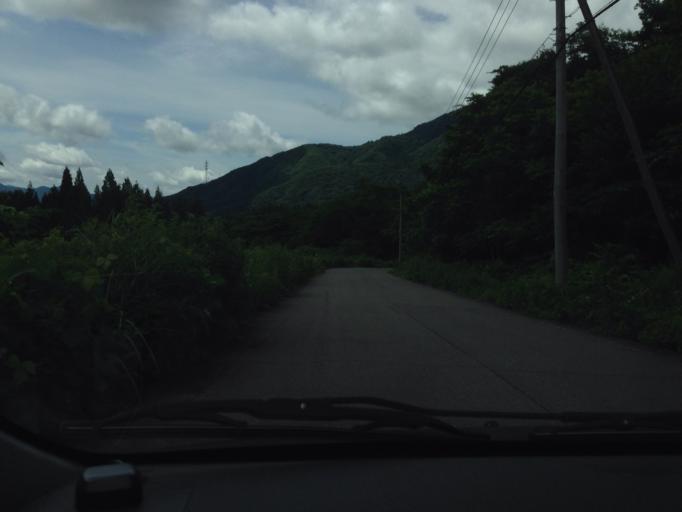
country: JP
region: Fukushima
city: Kitakata
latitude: 37.3066
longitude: 139.8501
